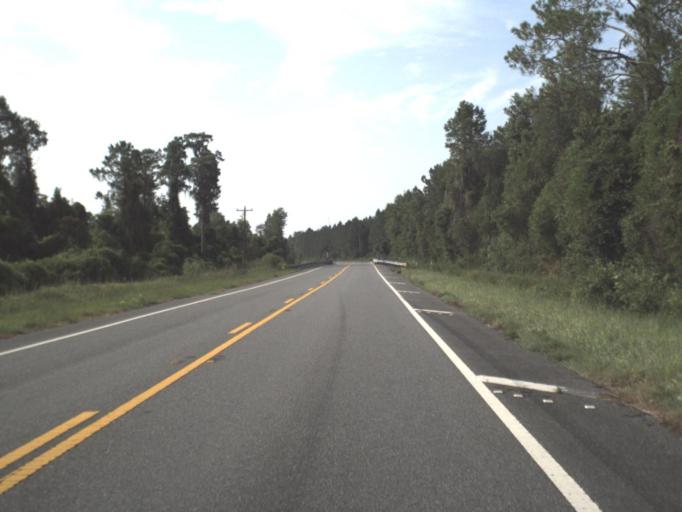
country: US
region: Florida
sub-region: Taylor County
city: Perry
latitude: 30.2174
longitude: -83.6137
